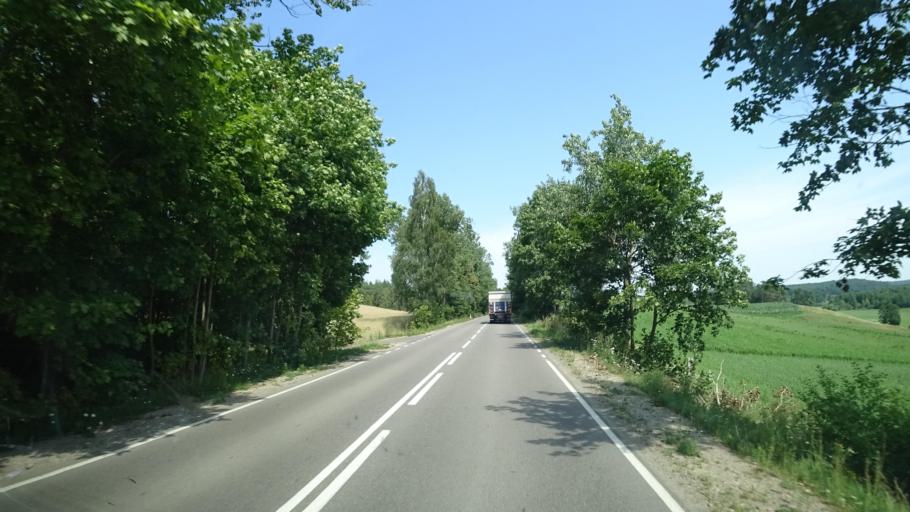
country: PL
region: Pomeranian Voivodeship
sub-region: Powiat koscierski
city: Lipusz
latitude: 54.0576
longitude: 17.8015
